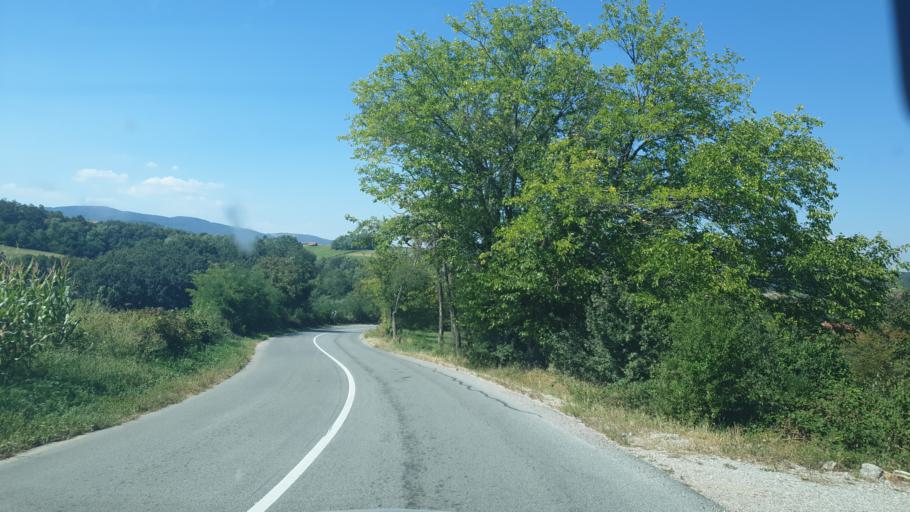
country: RS
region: Central Serbia
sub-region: Kolubarski Okrug
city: Mionica
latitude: 44.1804
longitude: 20.0356
